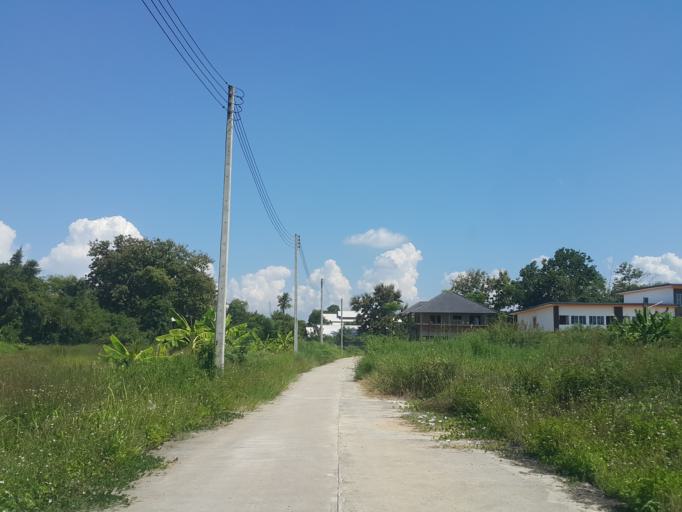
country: TH
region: Chiang Mai
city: Saraphi
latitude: 18.7677
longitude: 99.0485
